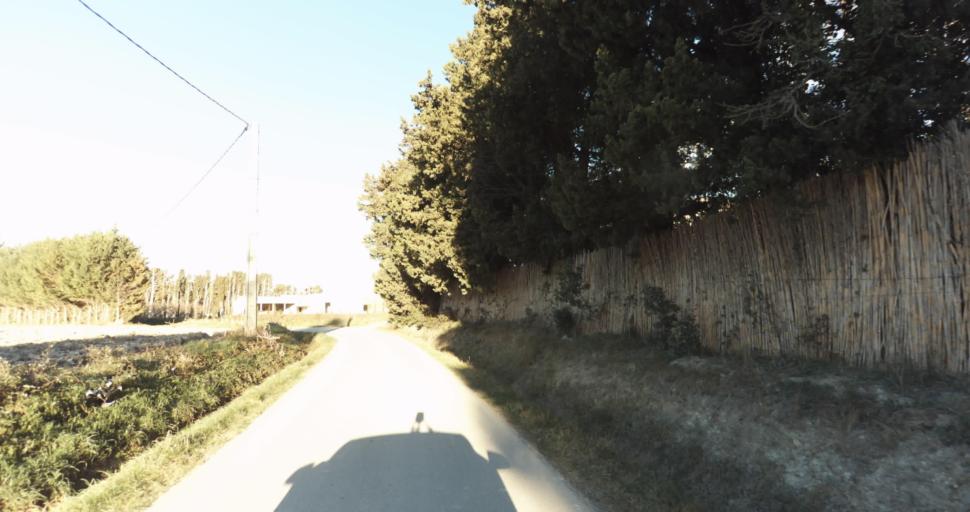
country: FR
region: Provence-Alpes-Cote d'Azur
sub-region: Departement des Bouches-du-Rhone
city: Barbentane
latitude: 43.9108
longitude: 4.7477
